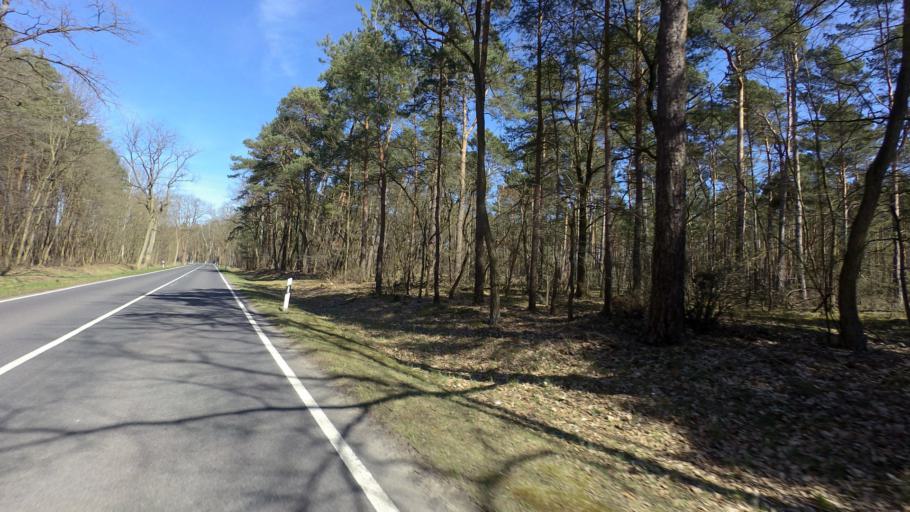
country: DE
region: Brandenburg
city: Storkow
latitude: 52.1995
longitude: 13.9229
